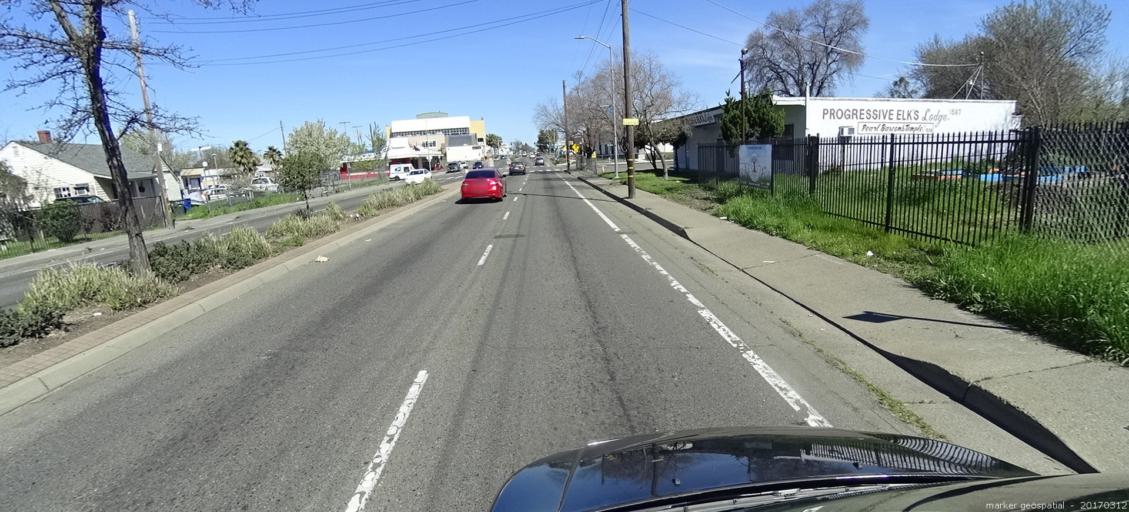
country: US
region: California
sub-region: Sacramento County
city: Rio Linda
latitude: 38.6339
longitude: -121.4303
